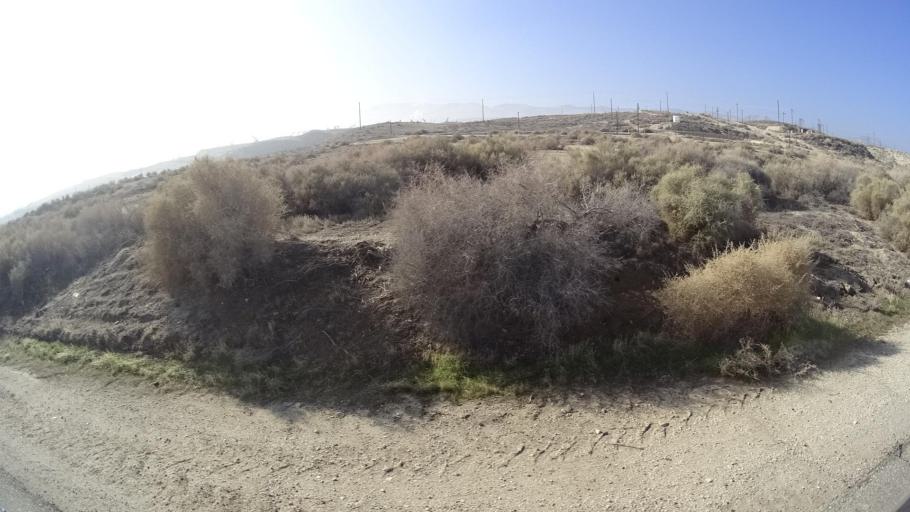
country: US
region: California
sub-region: Kern County
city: Taft Heights
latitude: 35.1623
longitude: -119.5262
